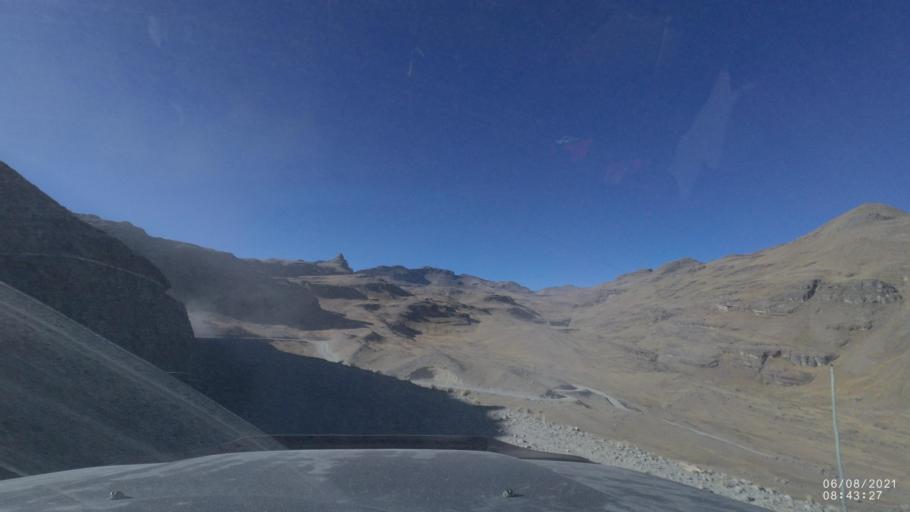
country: BO
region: Cochabamba
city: Sipe Sipe
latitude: -17.1690
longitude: -66.4115
